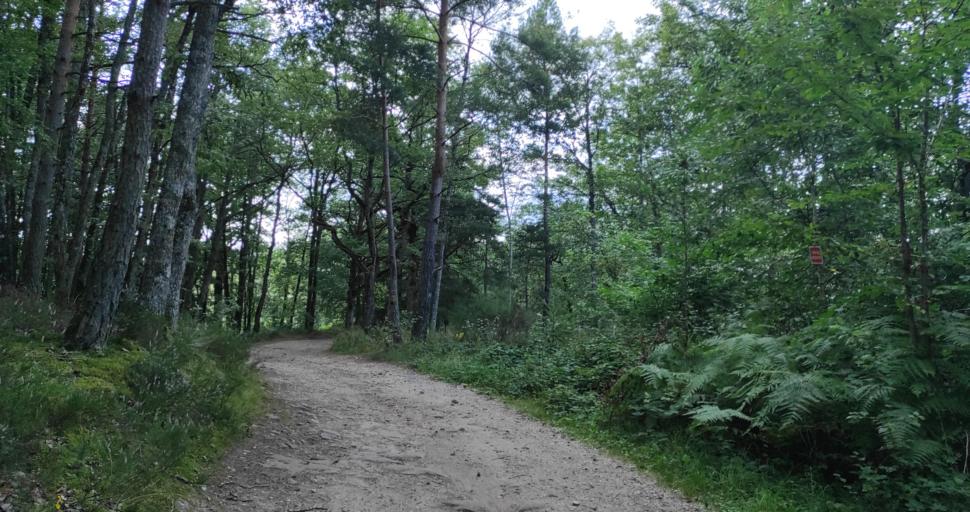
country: FR
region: Midi-Pyrenees
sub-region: Departement de l'Aveyron
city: La Loubiere
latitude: 44.3835
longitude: 2.7192
